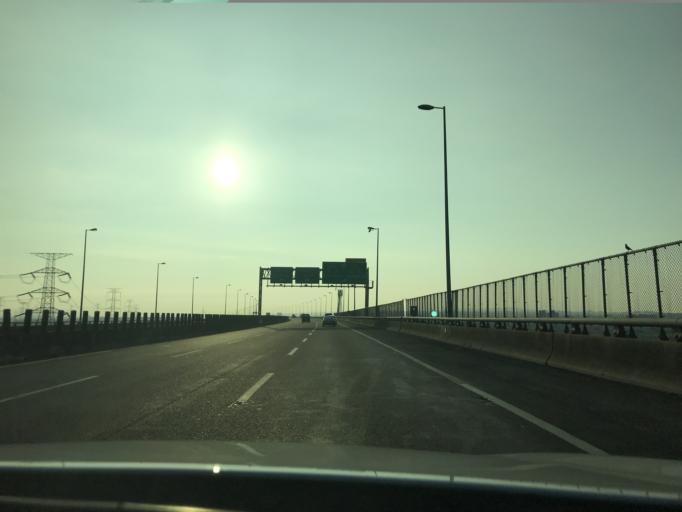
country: TW
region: Taiwan
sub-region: Changhua
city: Chang-hua
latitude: 24.1124
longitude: 120.5439
